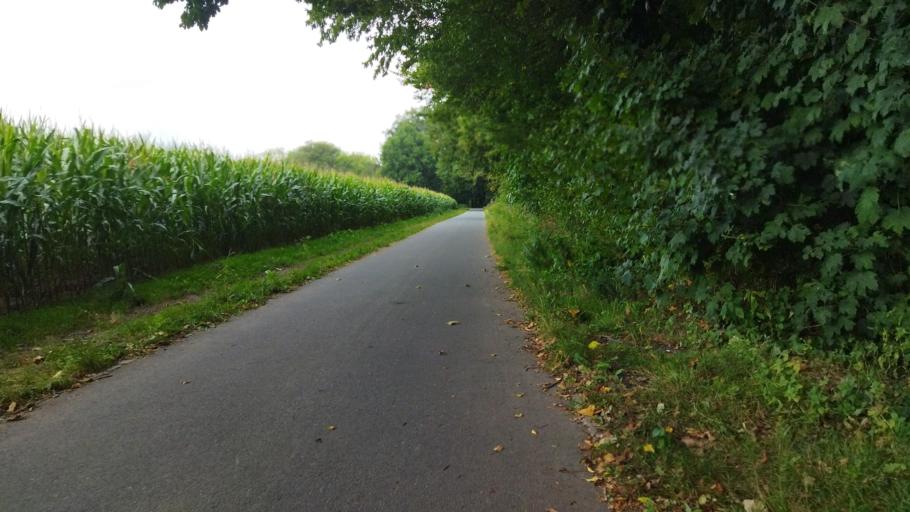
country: DE
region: North Rhine-Westphalia
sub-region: Regierungsbezirk Munster
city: Telgte
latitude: 52.0137
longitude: 7.7638
